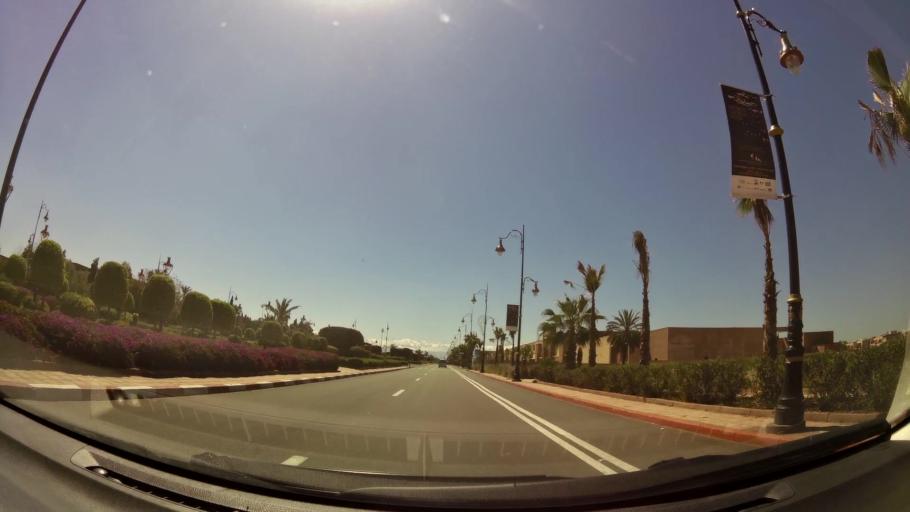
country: MA
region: Marrakech-Tensift-Al Haouz
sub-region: Marrakech
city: Marrakesh
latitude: 31.6077
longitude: -8.0018
